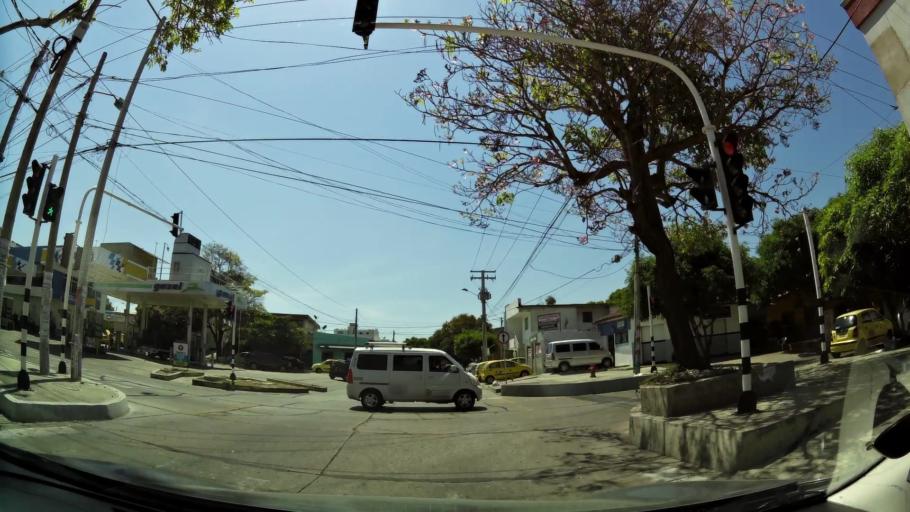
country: CO
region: Atlantico
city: Barranquilla
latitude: 10.9893
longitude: -74.7953
